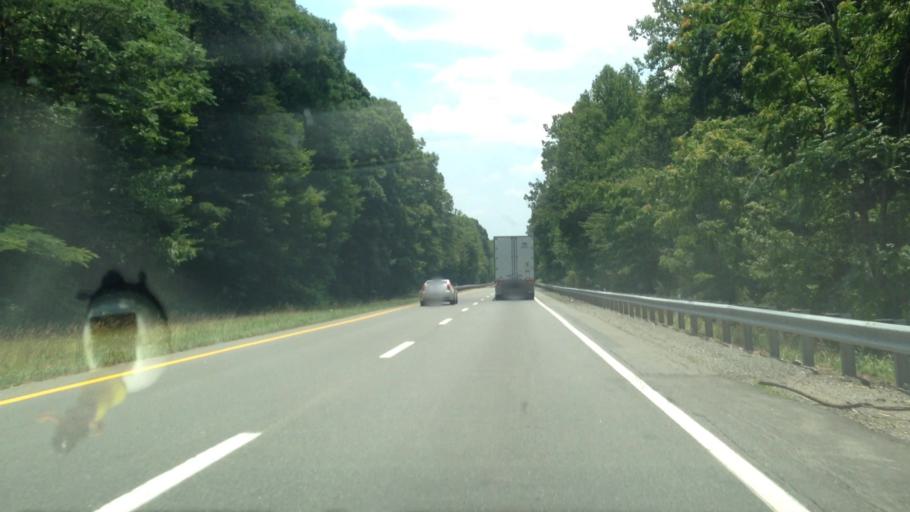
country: US
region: Virginia
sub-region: Henry County
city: Horse Pasture
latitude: 36.6425
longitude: -79.8998
